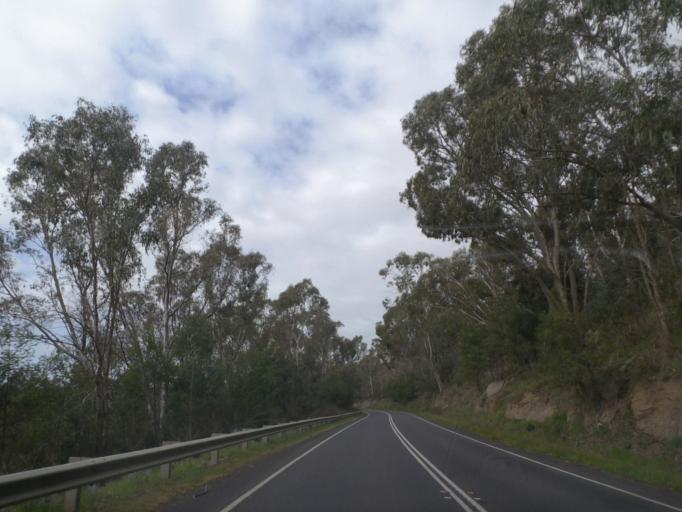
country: AU
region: Victoria
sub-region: Murrindindi
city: Kinglake West
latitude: -37.1407
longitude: 145.2371
